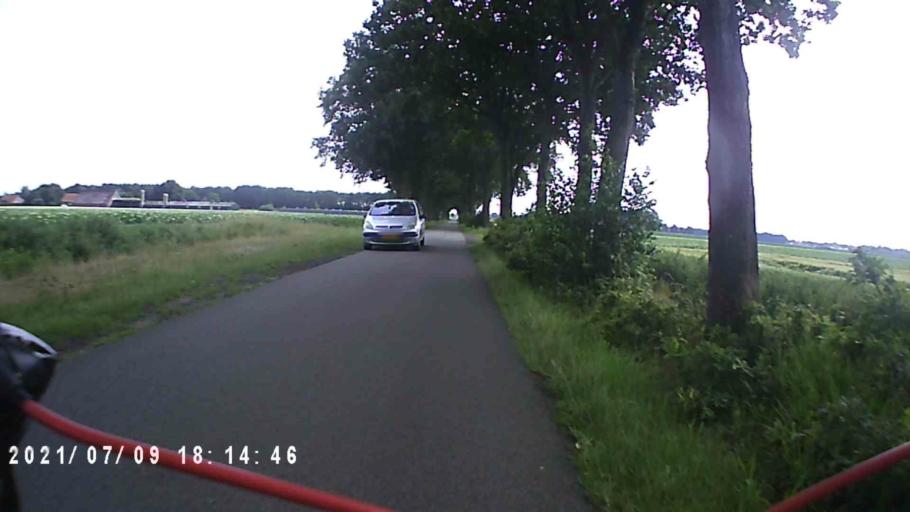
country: NL
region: Groningen
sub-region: Gemeente Pekela
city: Oude Pekela
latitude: 53.0588
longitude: 7.0221
